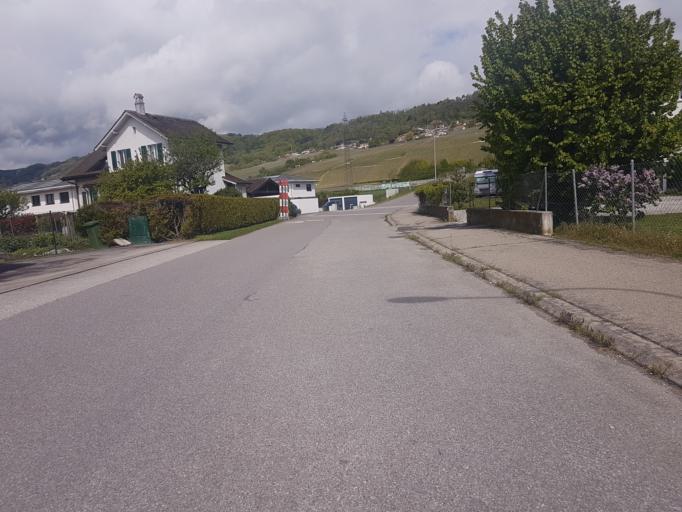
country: CH
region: Vaud
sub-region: Nyon District
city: Perroy
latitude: 46.4696
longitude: 6.3601
